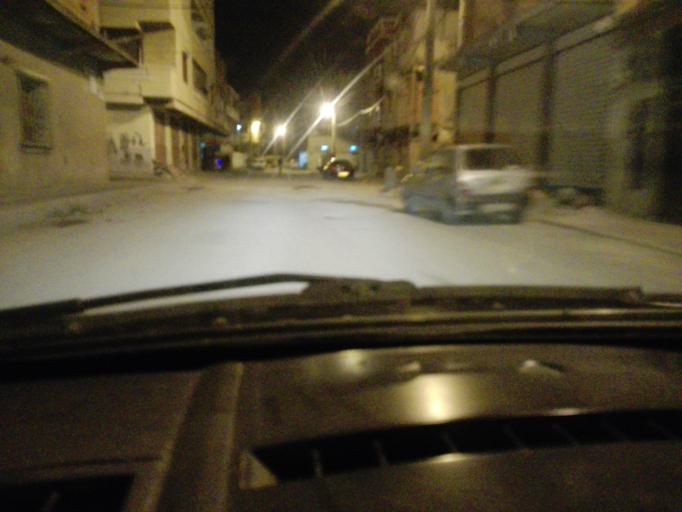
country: DZ
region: Alger
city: Dar el Beida
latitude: 36.7338
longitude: 3.2388
